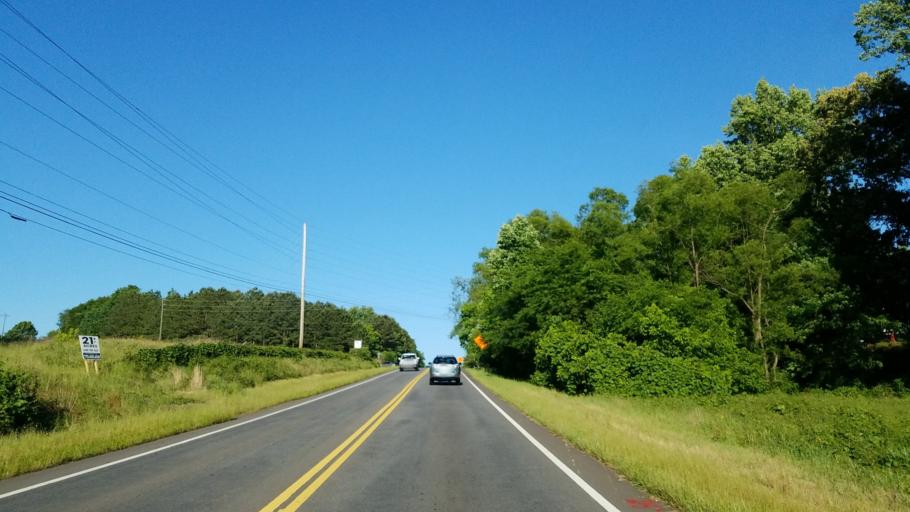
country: US
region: Georgia
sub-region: Cherokee County
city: Holly Springs
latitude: 34.1679
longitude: -84.4442
